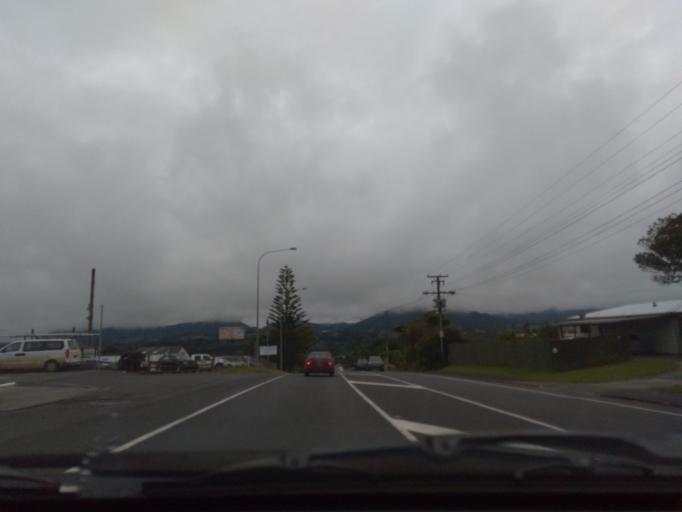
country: NZ
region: Auckland
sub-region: Auckland
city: Wellsford
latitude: -36.1719
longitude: 174.4475
